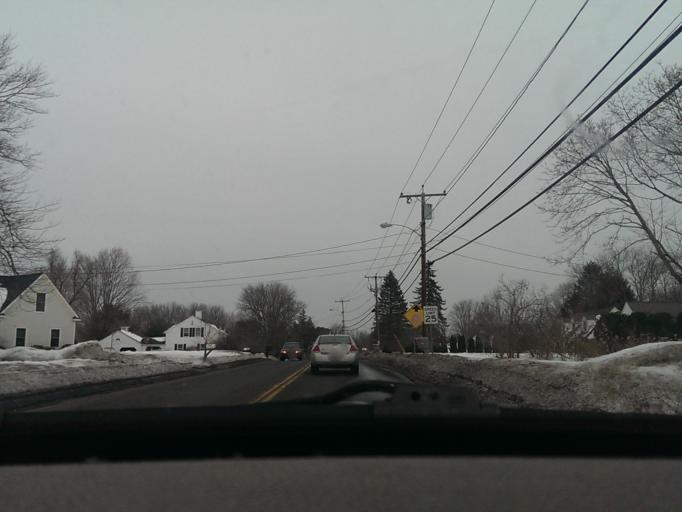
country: US
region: Massachusetts
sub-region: Hampden County
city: East Longmeadow
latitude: 42.0780
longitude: -72.4895
